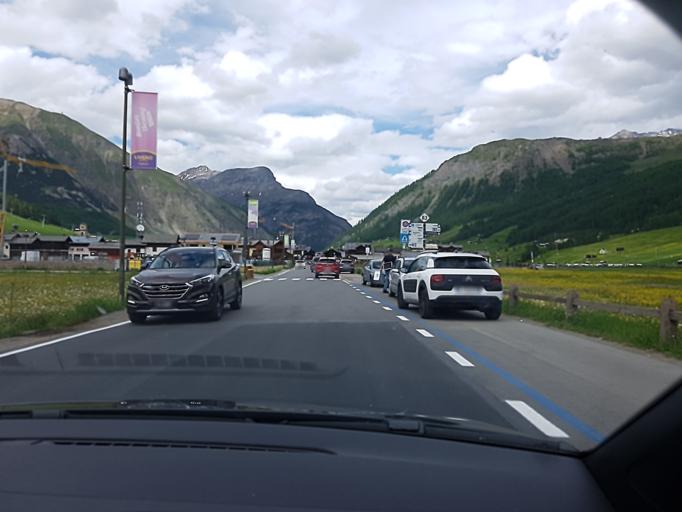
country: IT
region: Lombardy
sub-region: Provincia di Sondrio
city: Livigno
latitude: 46.5353
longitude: 10.1359
